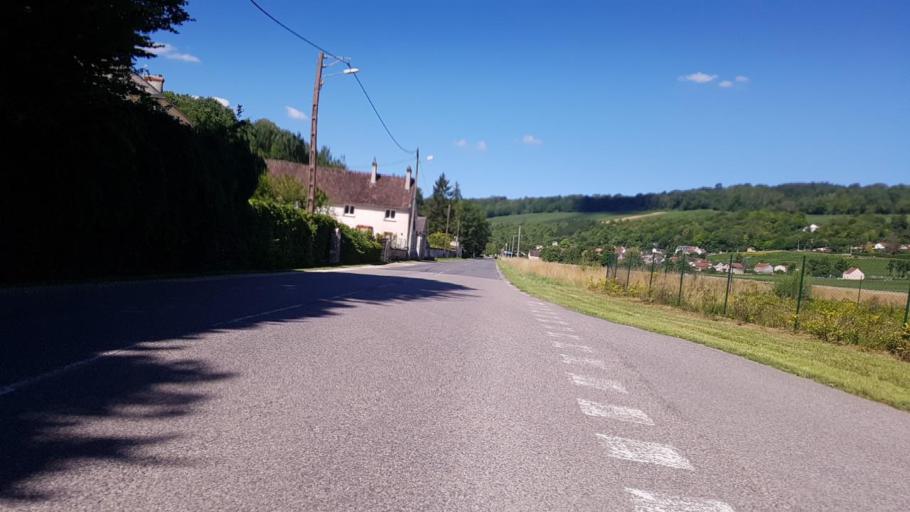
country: FR
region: Ile-de-France
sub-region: Departement de Seine-et-Marne
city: Saacy-sur-Marne
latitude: 48.9780
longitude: 3.2303
